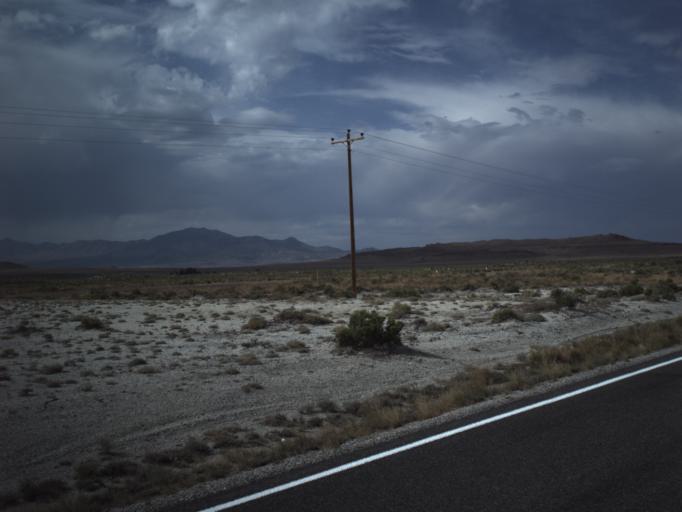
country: US
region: Utah
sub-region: Tooele County
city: Wendover
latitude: 41.4245
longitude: -113.8607
